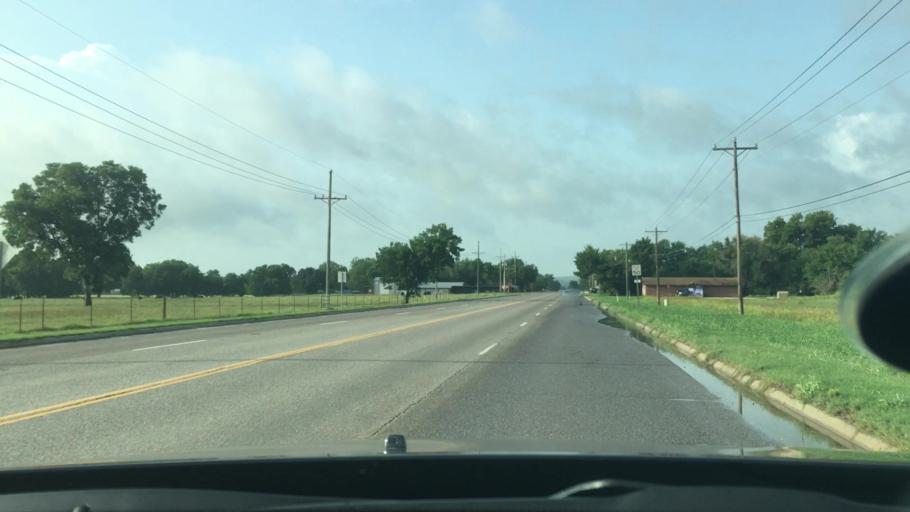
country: US
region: Oklahoma
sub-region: Murray County
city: Davis
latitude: 34.4843
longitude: -97.1306
